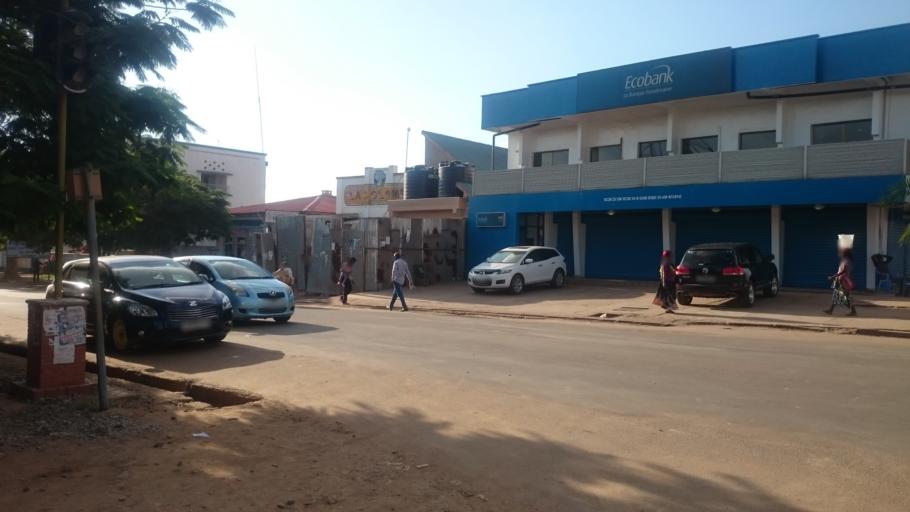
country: CD
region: Katanga
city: Lubumbashi
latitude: -11.6705
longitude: 27.4814
